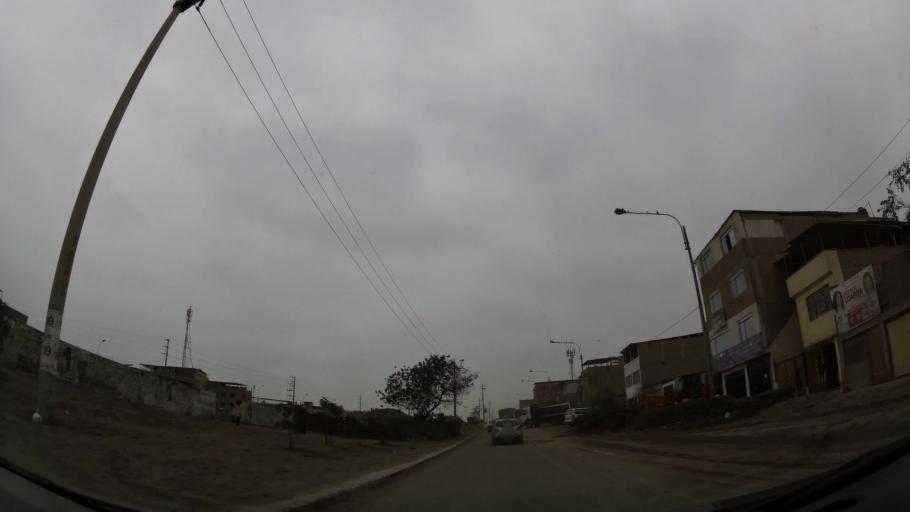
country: PE
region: Lima
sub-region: Lima
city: Surco
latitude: -12.2238
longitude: -76.9233
